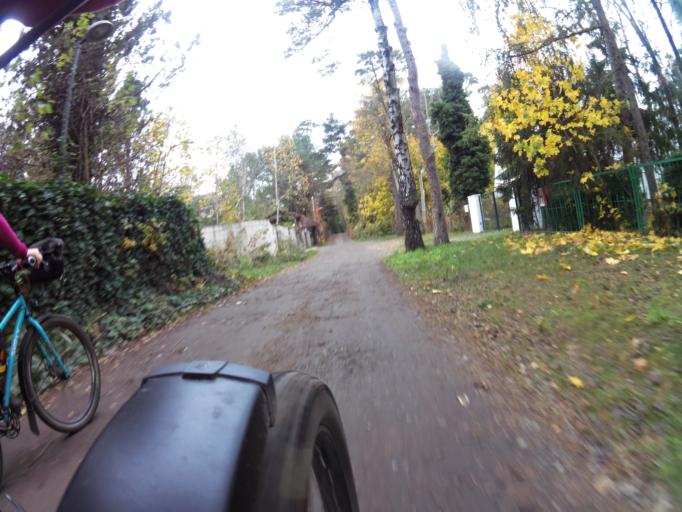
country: PL
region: Pomeranian Voivodeship
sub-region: Powiat pucki
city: Jastarnia
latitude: 54.6839
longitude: 18.7102
